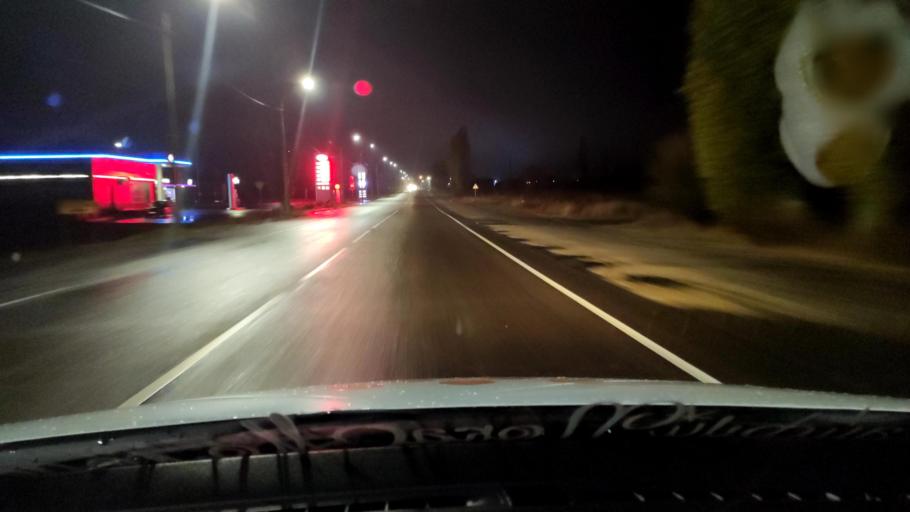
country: RU
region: Voronezj
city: Semiluki
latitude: 51.7196
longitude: 39.0325
